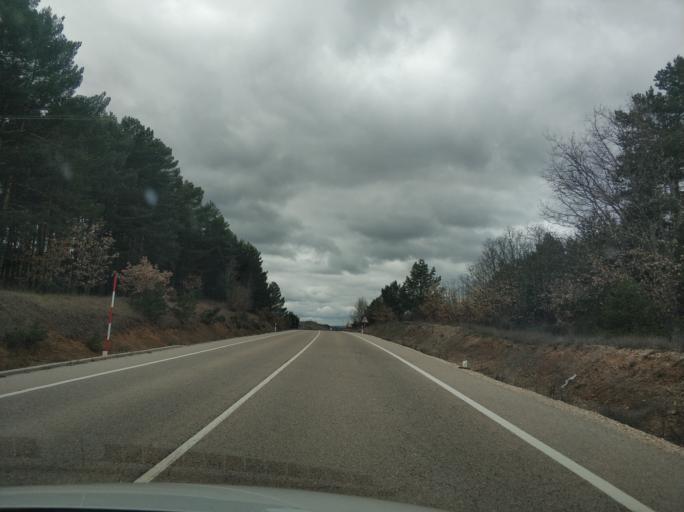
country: ES
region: Castille and Leon
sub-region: Provincia de Burgos
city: Cabezon de la Sierra
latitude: 41.8887
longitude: -3.2442
